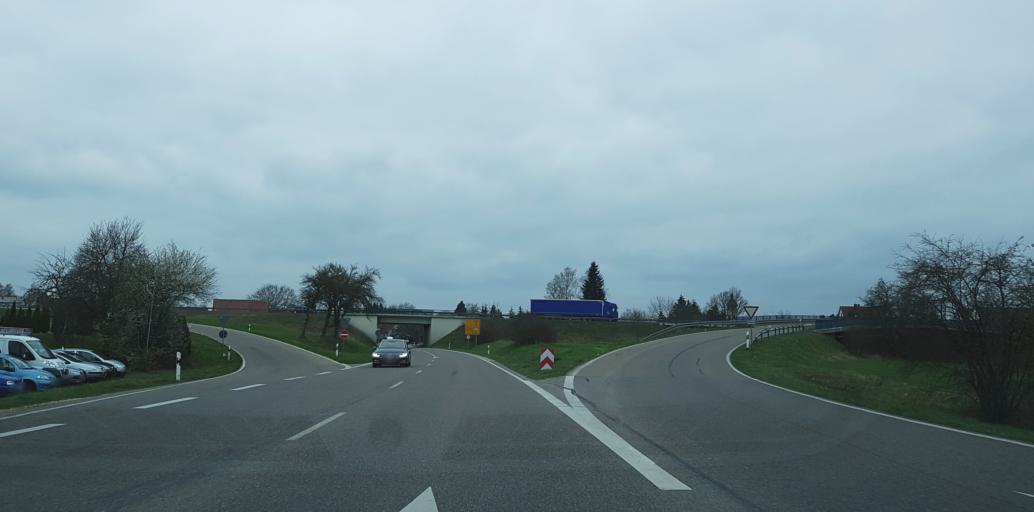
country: DE
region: Baden-Wuerttemberg
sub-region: Tuebingen Region
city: Ehingen
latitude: 48.2917
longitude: 9.7316
